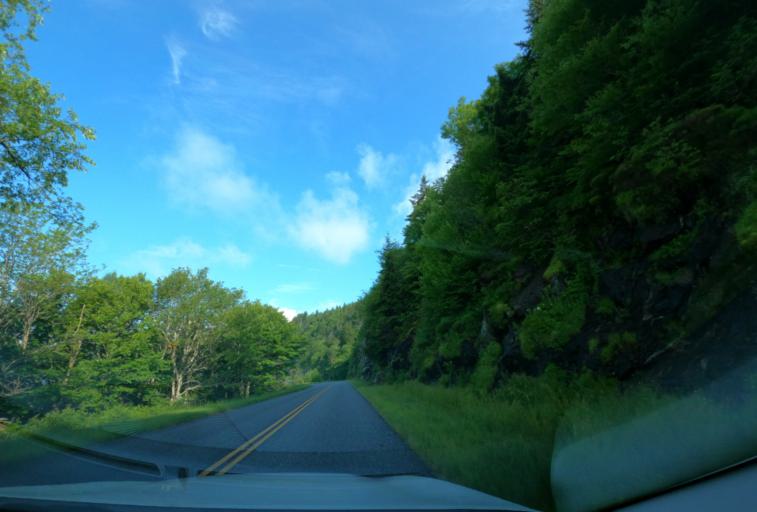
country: US
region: North Carolina
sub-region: Haywood County
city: Hazelwood
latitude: 35.3016
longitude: -82.9336
